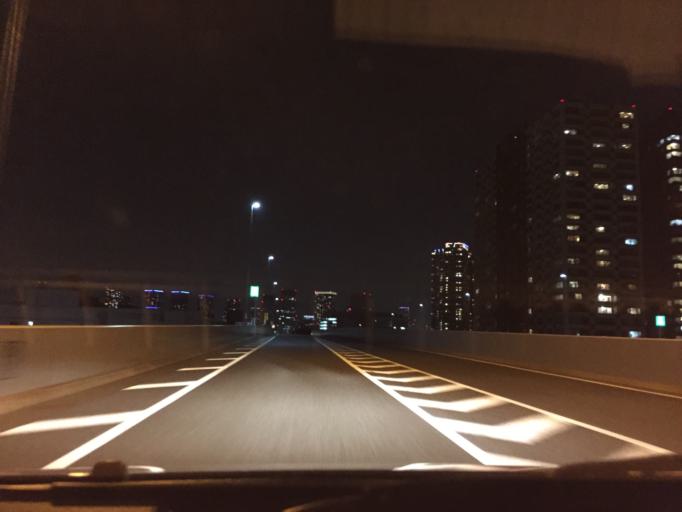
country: JP
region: Tokyo
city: Urayasu
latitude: 35.6399
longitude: 139.7954
